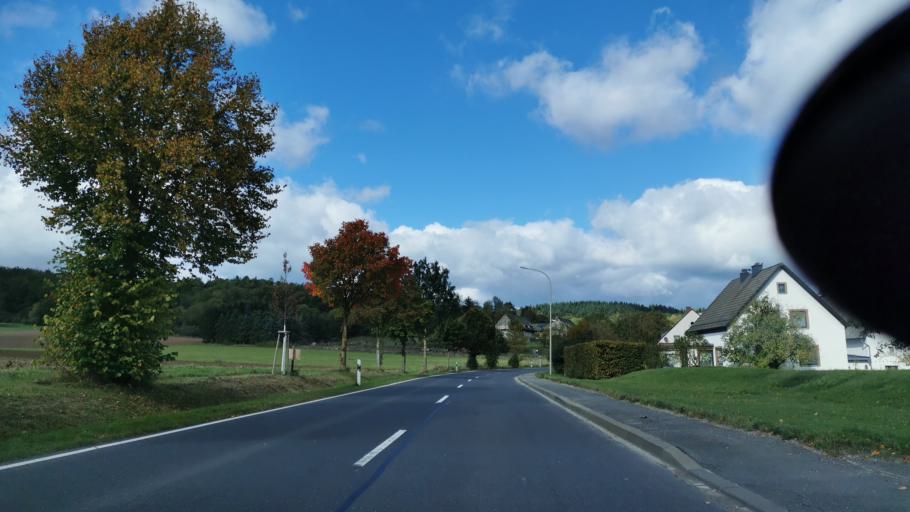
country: DE
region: Rheinland-Pfalz
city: Berndorf
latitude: 50.3142
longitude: 6.7255
